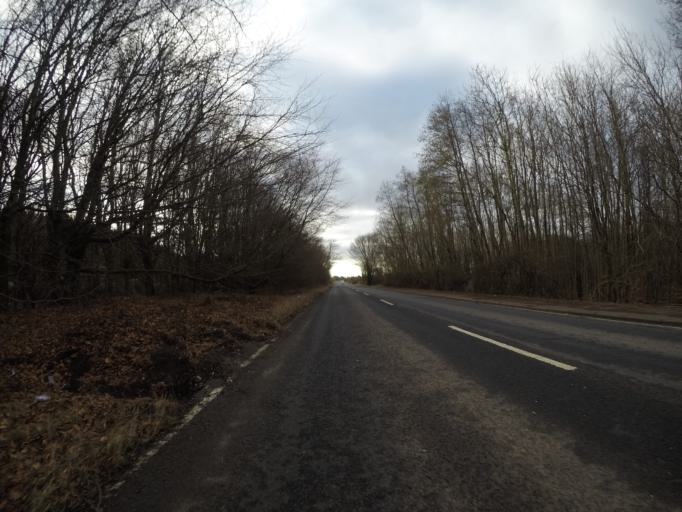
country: GB
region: Scotland
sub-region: North Ayrshire
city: Dreghorn
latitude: 55.5788
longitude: -4.6431
